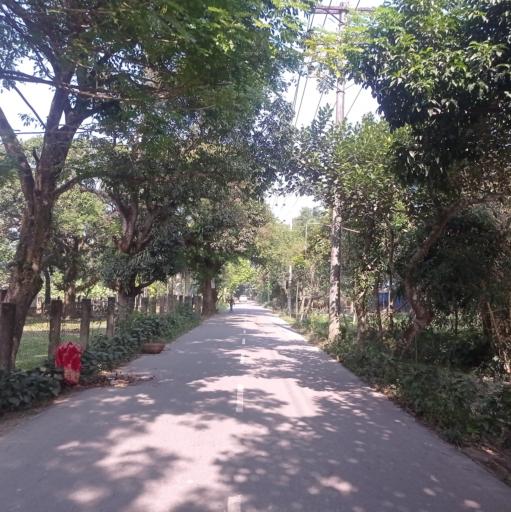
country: BD
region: Dhaka
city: Narsingdi
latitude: 24.0737
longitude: 90.6932
